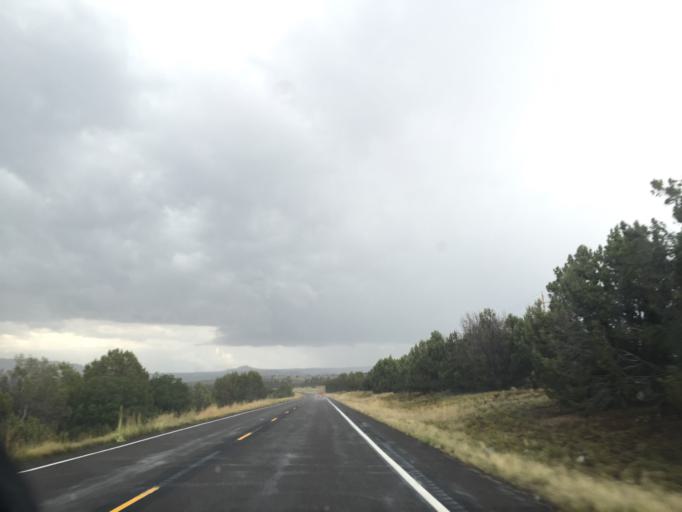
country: US
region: Utah
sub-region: Kane County
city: Kanab
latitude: 37.2423
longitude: -112.7521
